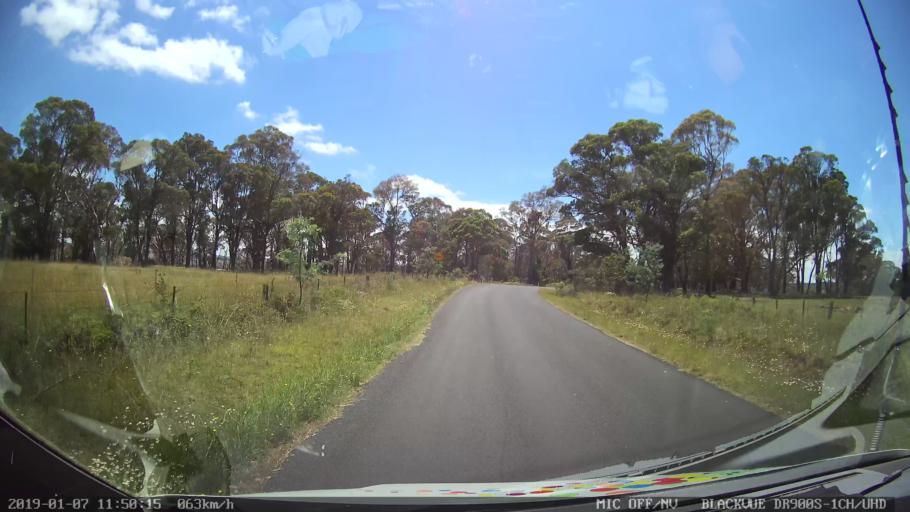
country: AU
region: New South Wales
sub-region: Guyra
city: Guyra
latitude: -30.3130
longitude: 151.6340
